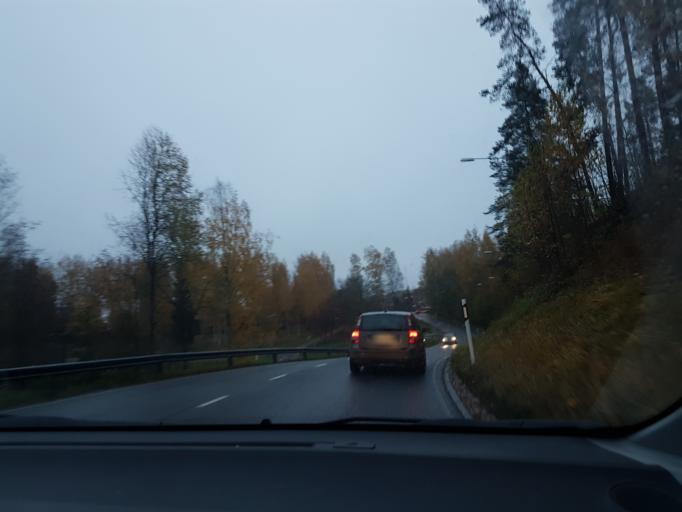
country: FI
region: Uusimaa
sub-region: Helsinki
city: Tuusula
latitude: 60.4043
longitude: 25.0197
